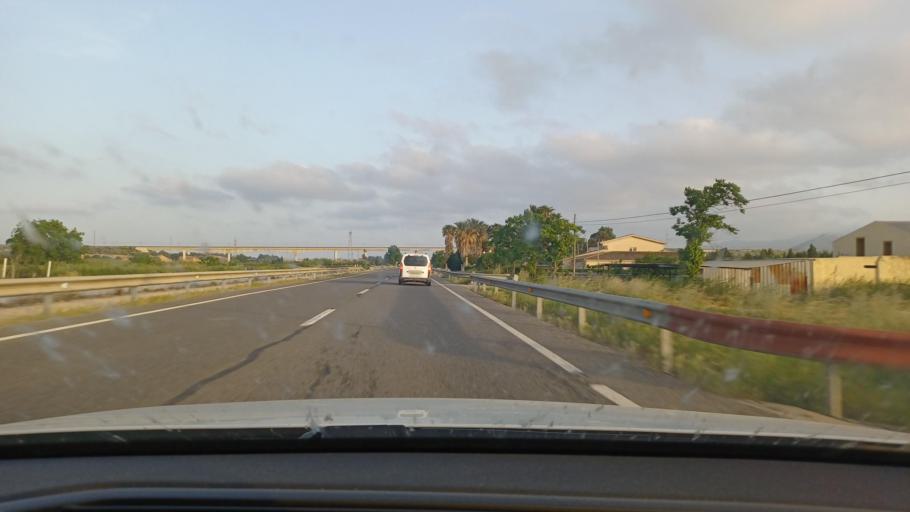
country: ES
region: Catalonia
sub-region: Provincia de Tarragona
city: Amposta
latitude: 40.7381
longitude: 0.5663
